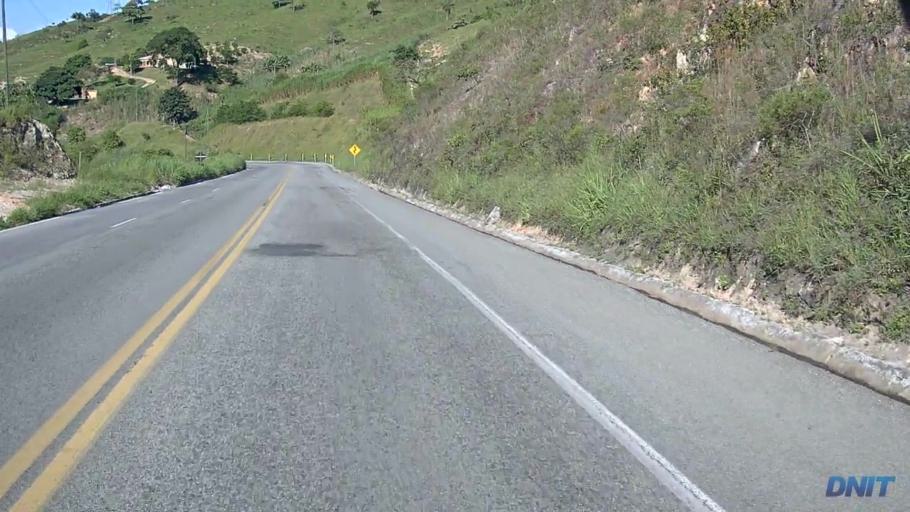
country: BR
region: Minas Gerais
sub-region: Nova Era
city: Nova Era
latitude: -19.6511
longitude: -42.9364
